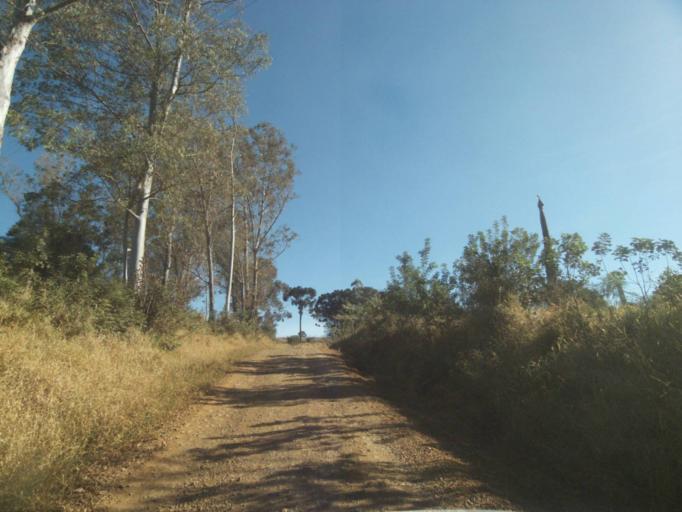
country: BR
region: Parana
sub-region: Tibagi
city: Tibagi
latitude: -24.5412
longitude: -50.5037
